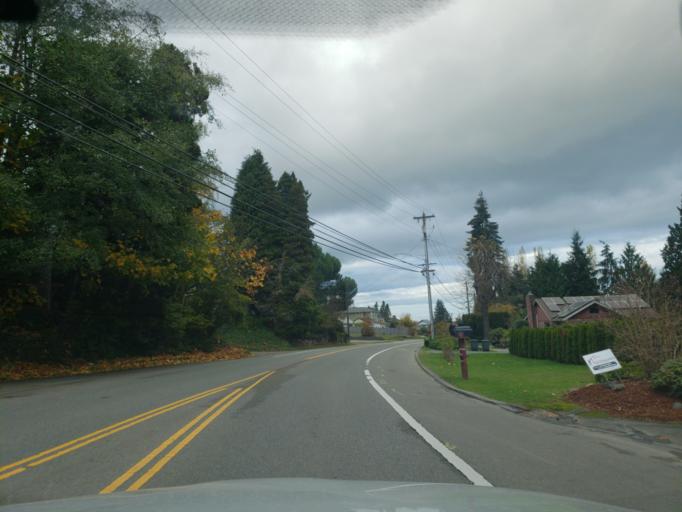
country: US
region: Washington
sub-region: Snohomish County
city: Everett
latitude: 47.9576
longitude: -122.2409
